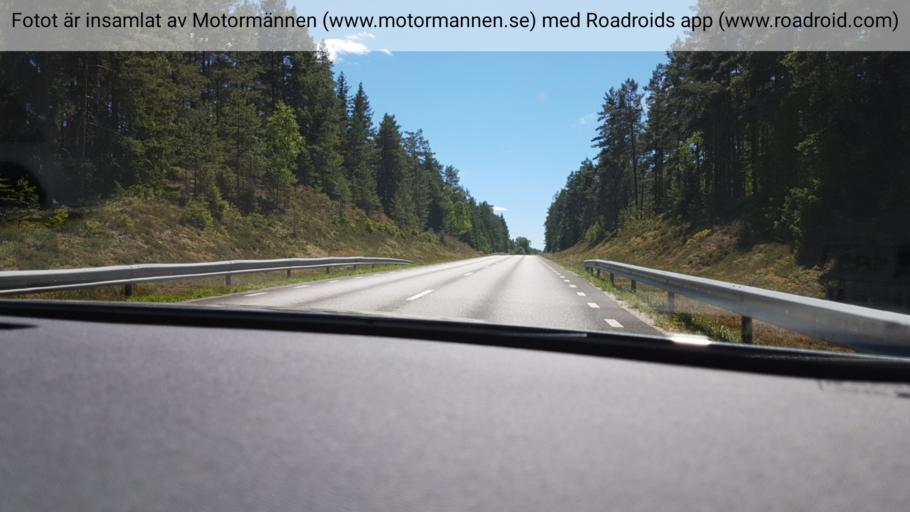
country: SE
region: Joenkoeping
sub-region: Gnosjo Kommun
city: Gnosjoe
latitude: 57.5460
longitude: 13.6903
